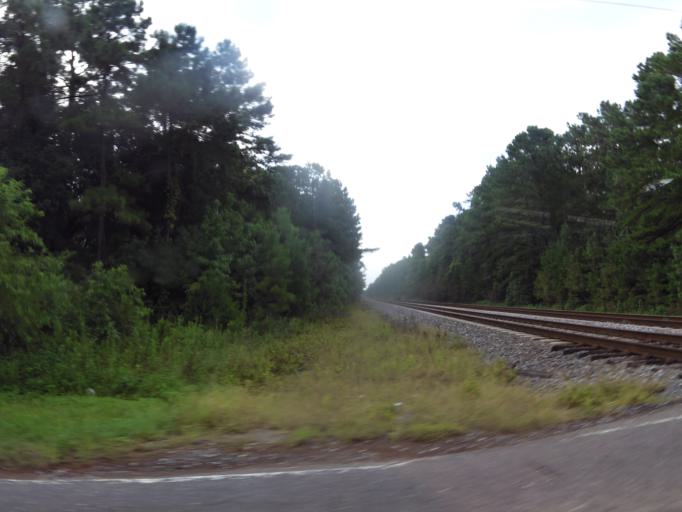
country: US
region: Florida
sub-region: Nassau County
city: Nassau Village-Ratliff
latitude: 30.4324
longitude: -81.7666
